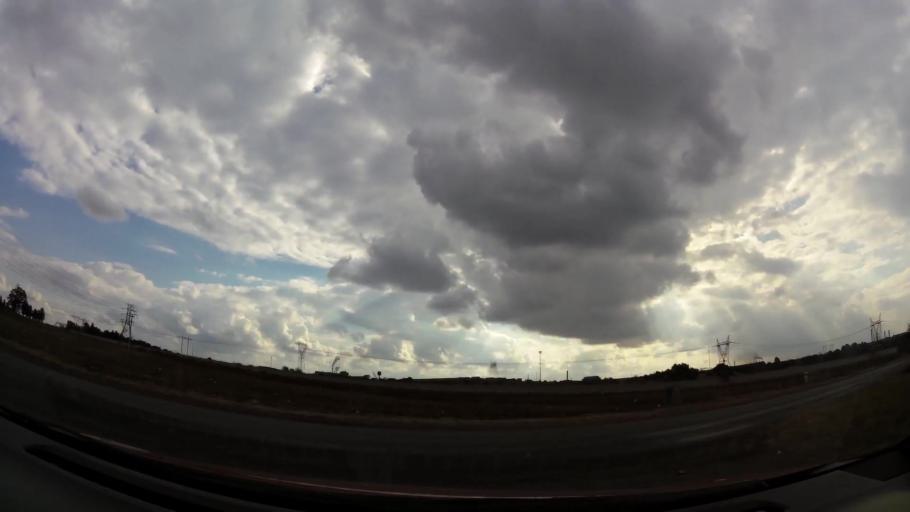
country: ZA
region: Gauteng
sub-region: Sedibeng District Municipality
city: Vanderbijlpark
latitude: -26.6712
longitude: 27.8376
